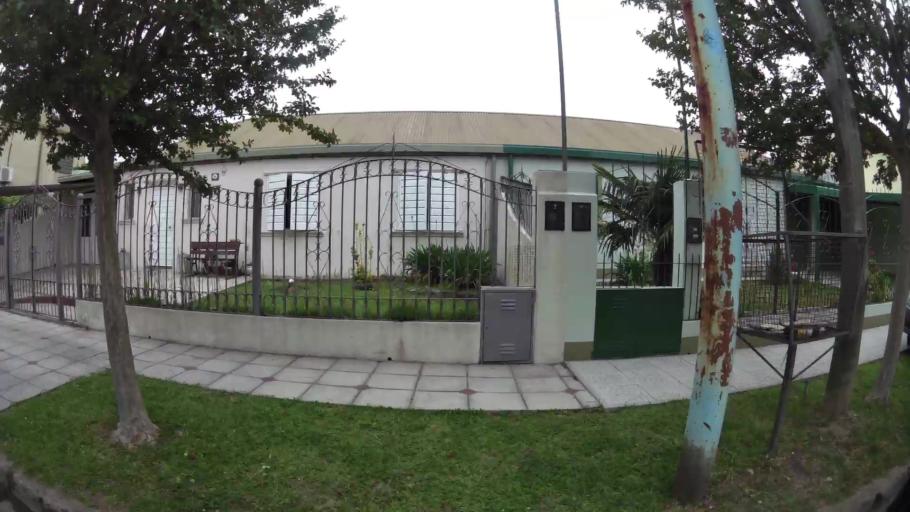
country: AR
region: Buenos Aires
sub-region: Partido de Campana
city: Campana
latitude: -34.1996
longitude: -58.9394
